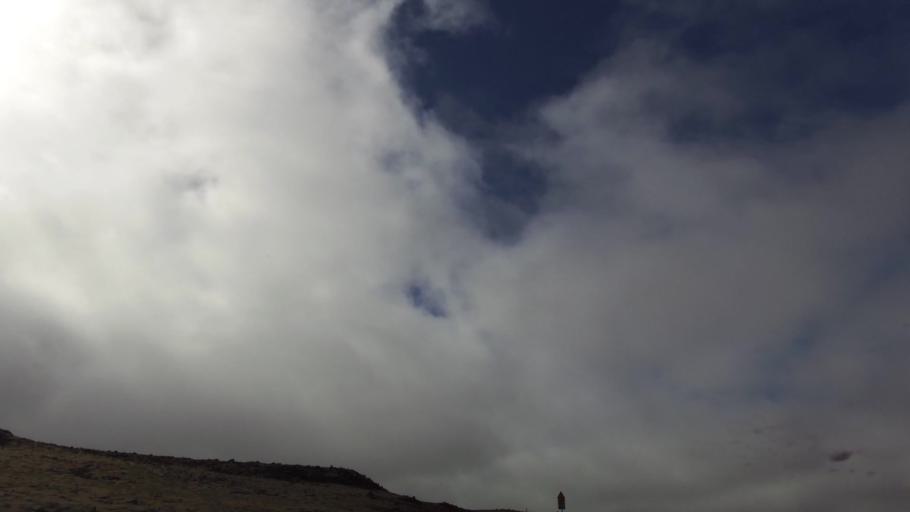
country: IS
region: West
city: Olafsvik
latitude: 65.5439
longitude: -24.3141
